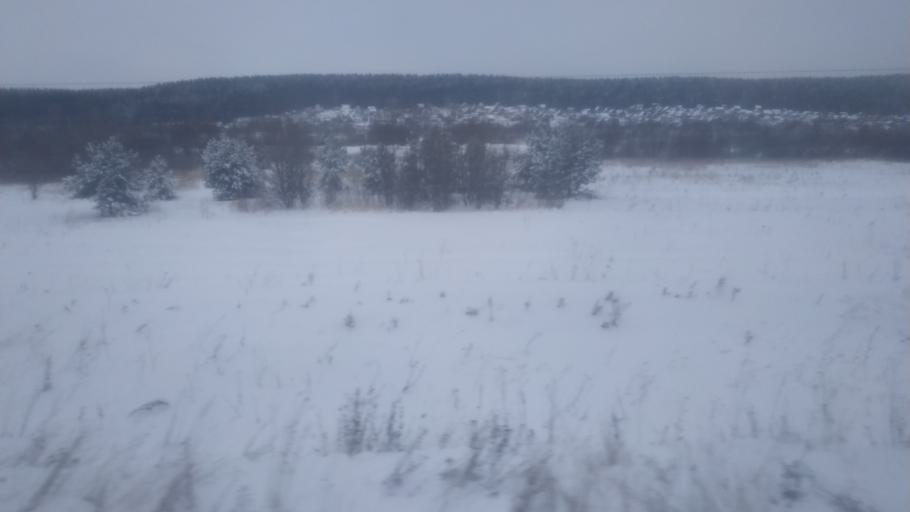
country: RU
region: Udmurtiya
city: Sigayevo
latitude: 56.4535
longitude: 53.6833
